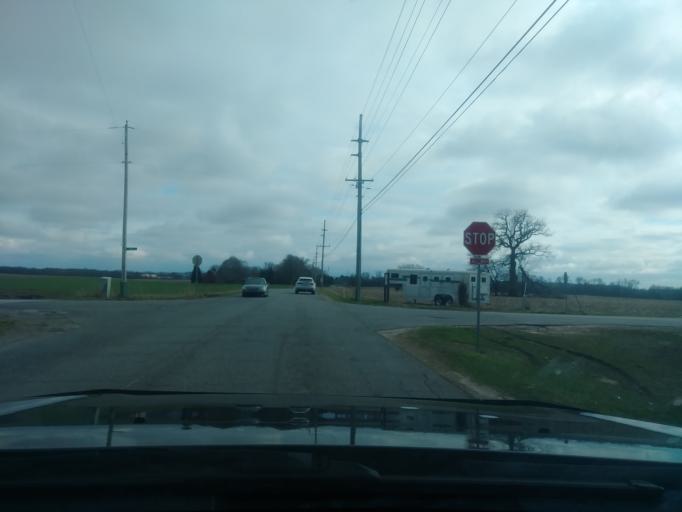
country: US
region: Indiana
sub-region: LaPorte County
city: LaPorte
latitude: 41.6107
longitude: -86.7973
